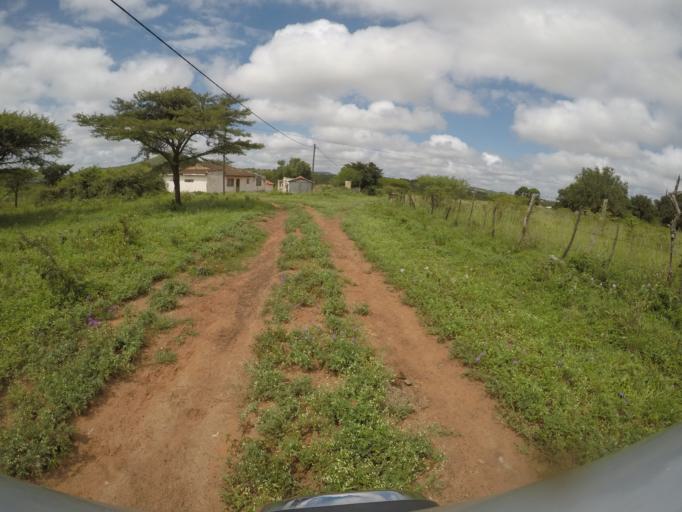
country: ZA
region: KwaZulu-Natal
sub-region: uThungulu District Municipality
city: Empangeni
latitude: -28.5859
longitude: 31.8482
